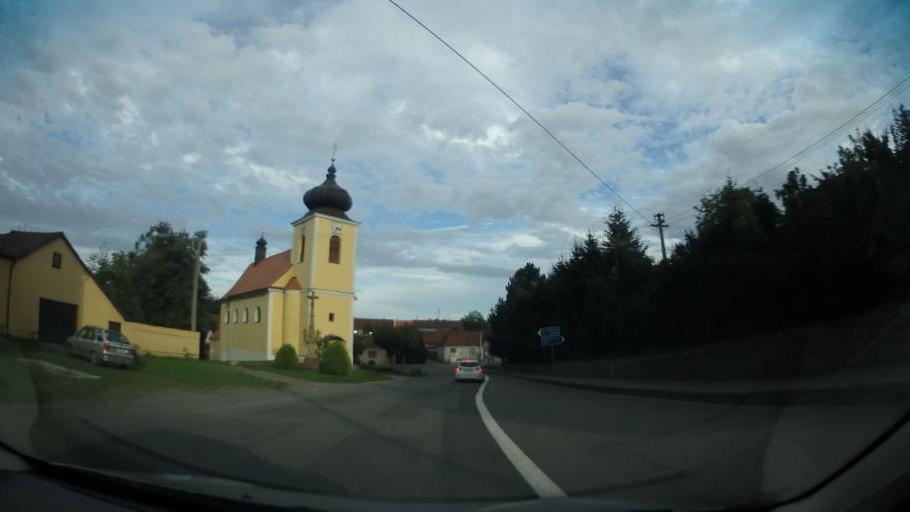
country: CZ
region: Olomoucky
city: Horni Stepanov
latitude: 49.5493
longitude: 16.7894
